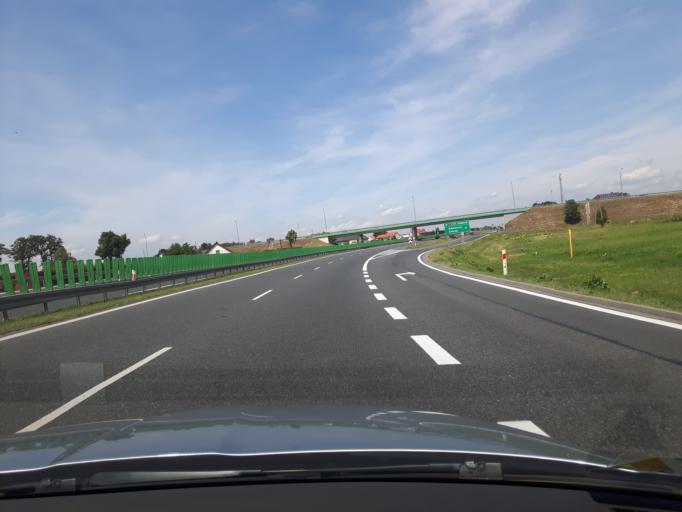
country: PL
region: Masovian Voivodeship
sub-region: Powiat plonski
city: Zaluski
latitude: 52.5094
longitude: 20.5294
